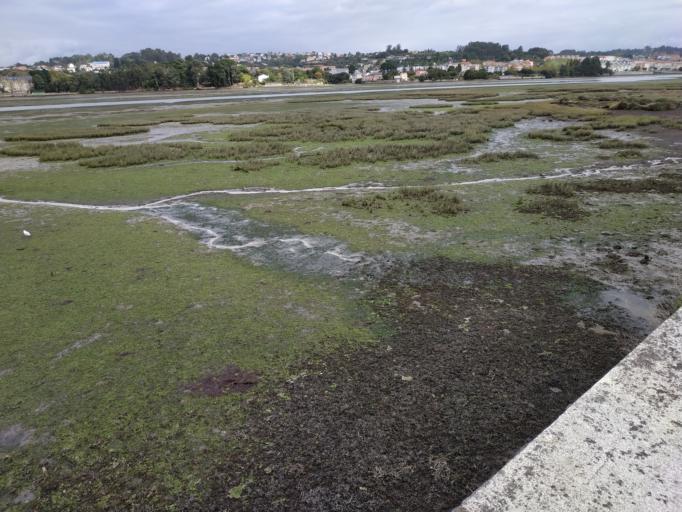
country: ES
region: Galicia
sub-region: Provincia da Coruna
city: Culleredo
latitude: 43.3233
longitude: -8.3762
